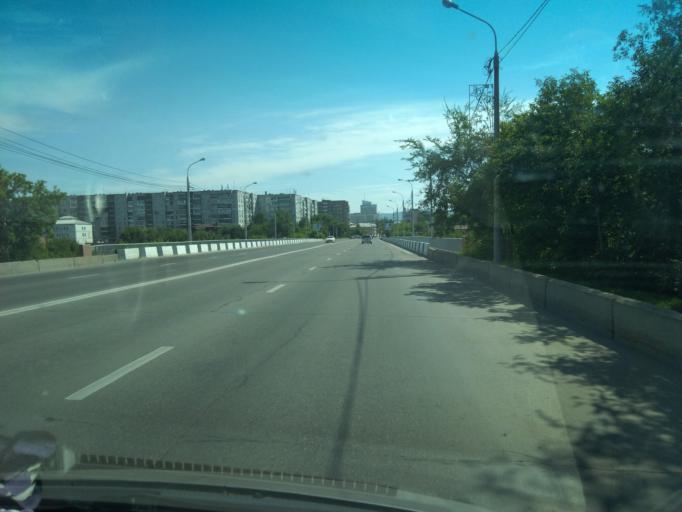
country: RU
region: Krasnoyarskiy
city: Krasnoyarsk
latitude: 56.0185
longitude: 92.8694
